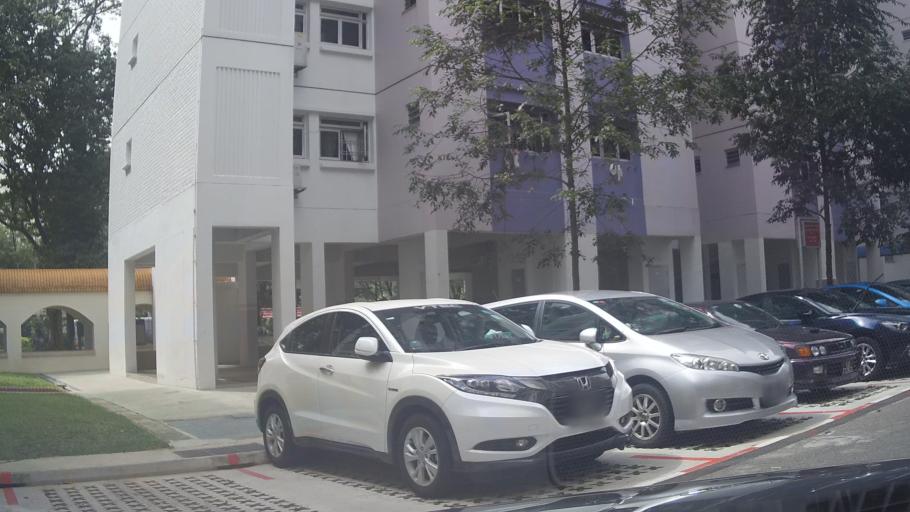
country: MY
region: Johor
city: Johor Bahru
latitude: 1.4399
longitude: 103.7911
